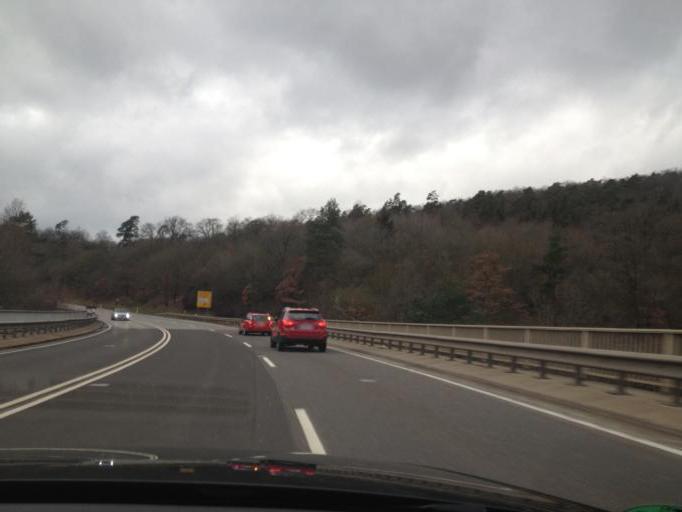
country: DE
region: Rheinland-Pfalz
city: Idar-Oberstein
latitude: 49.7030
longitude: 7.3034
